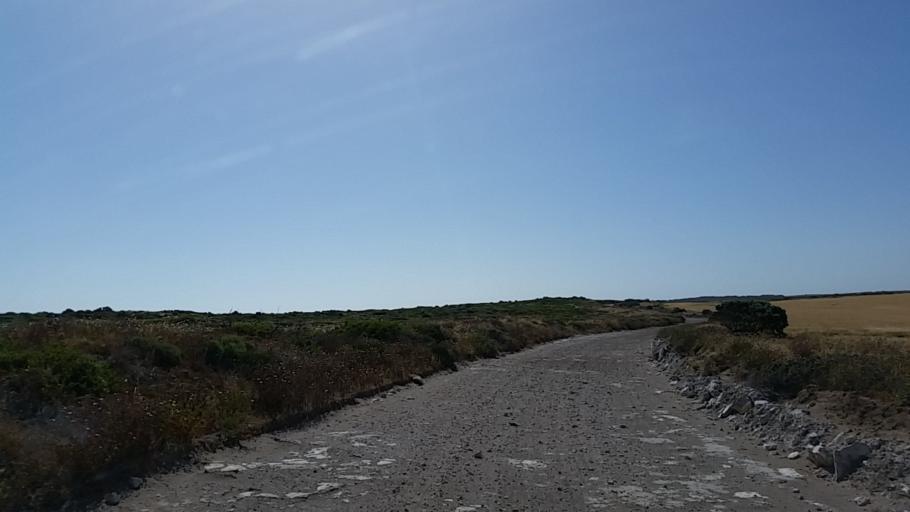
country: AU
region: South Australia
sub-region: Yorke Peninsula
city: Honiton
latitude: -35.2402
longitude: 137.1321
